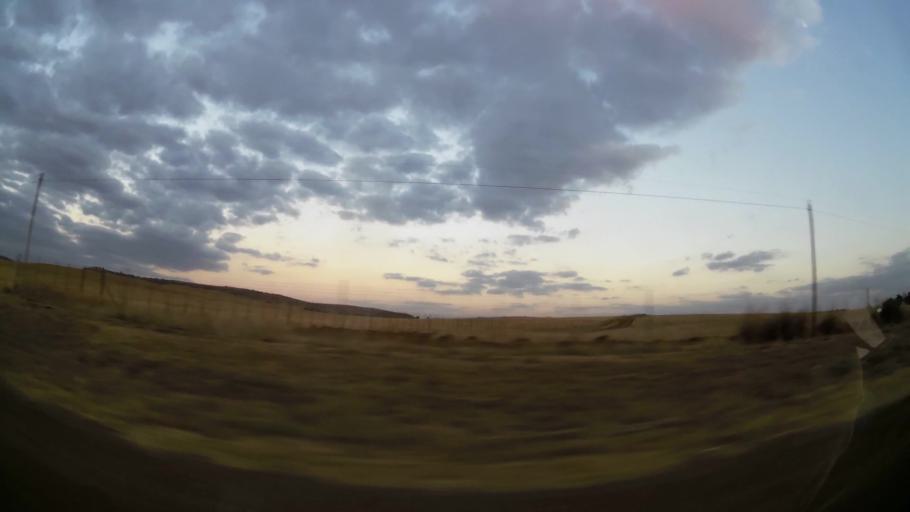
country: ZA
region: Gauteng
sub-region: West Rand District Municipality
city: Krugersdorp
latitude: -26.0540
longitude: 27.7084
